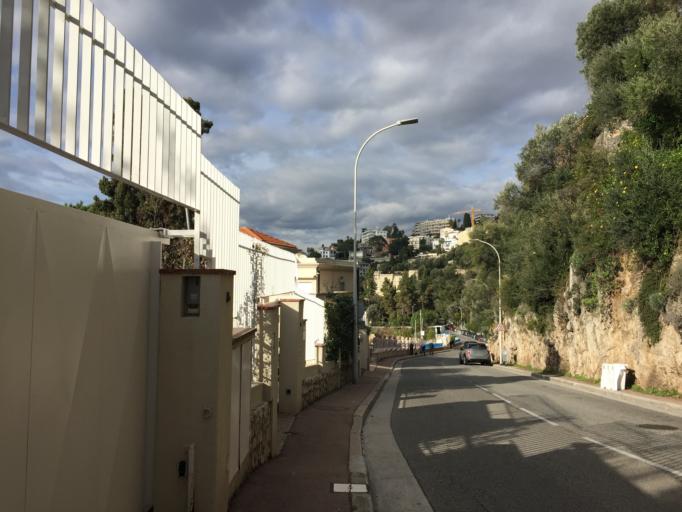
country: FR
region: Provence-Alpes-Cote d'Azur
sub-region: Departement des Alpes-Maritimes
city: Villefranche-sur-Mer
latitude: 43.6877
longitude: 7.2945
